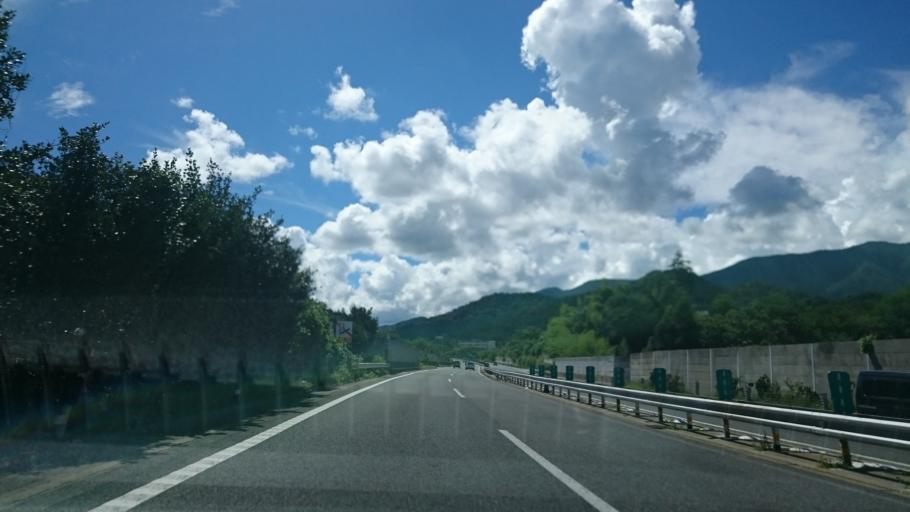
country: JP
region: Nagano
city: Iida
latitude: 35.4872
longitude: 137.7833
